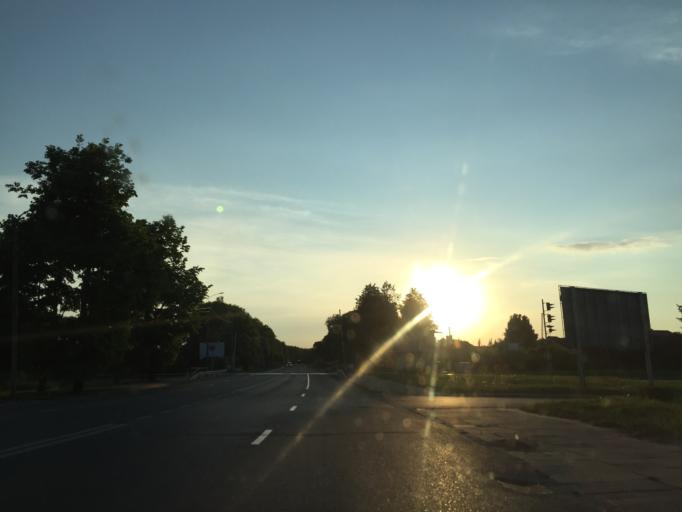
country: LT
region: Siauliu apskritis
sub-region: Siauliai
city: Siauliai
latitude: 55.9434
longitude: 23.2829
